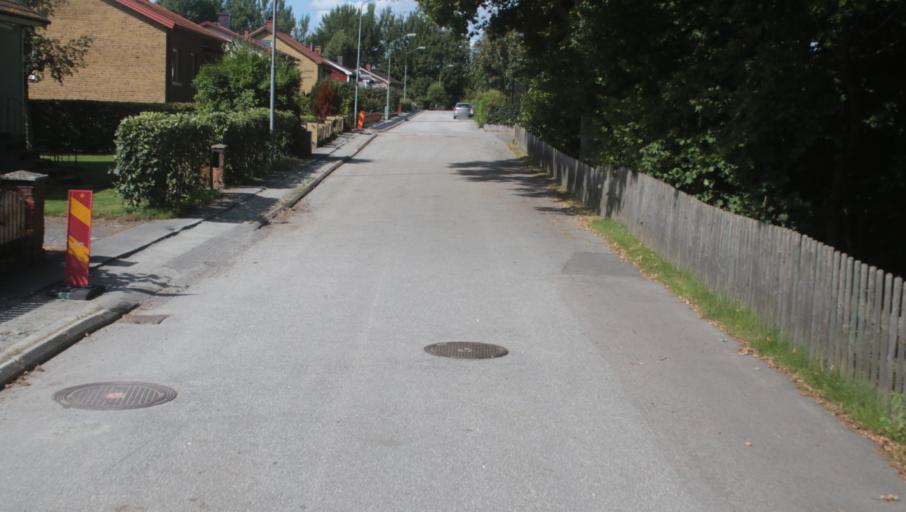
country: SE
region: Blekinge
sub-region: Karlshamns Kommun
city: Karlshamn
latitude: 56.2116
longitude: 14.8289
